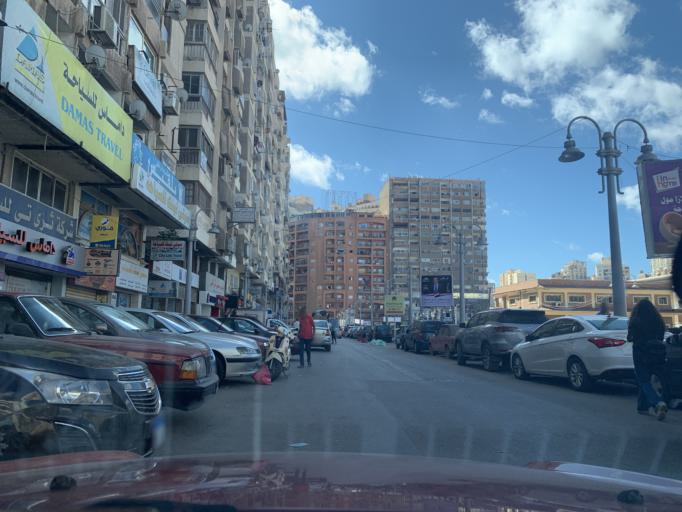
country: EG
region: Alexandria
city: Alexandria
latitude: 31.2187
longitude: 29.9438
